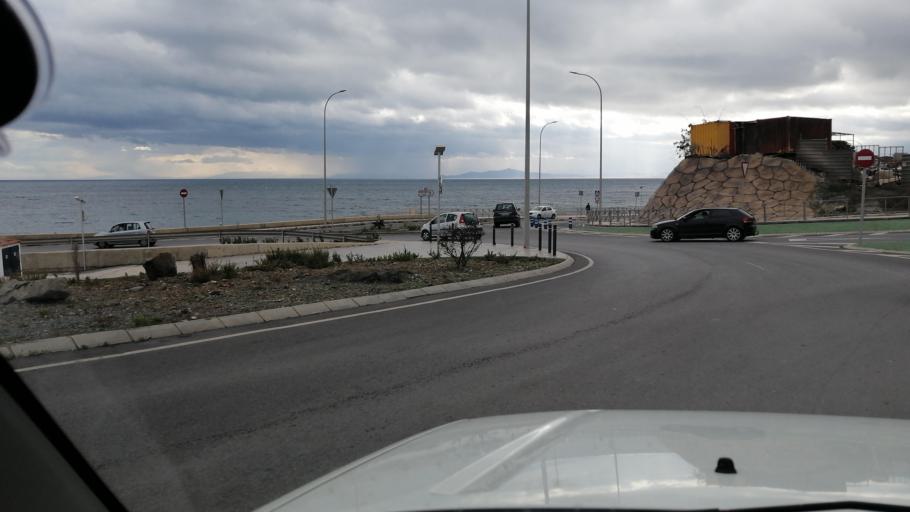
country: ES
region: Ceuta
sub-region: Ceuta
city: Ceuta
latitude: 35.8768
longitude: -5.3412
